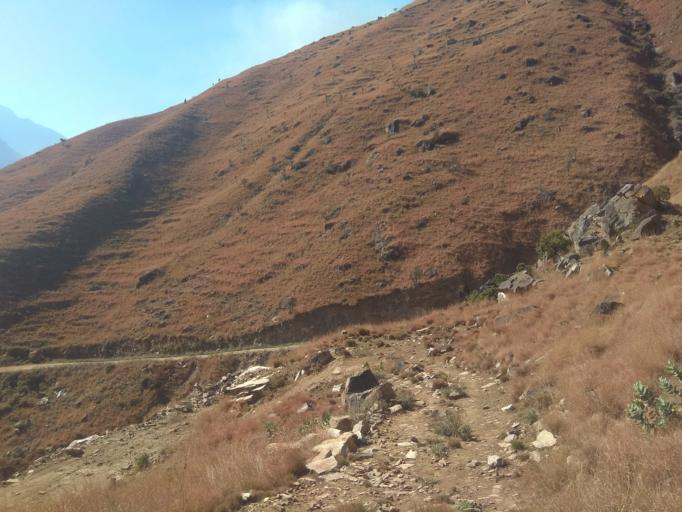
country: NP
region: Mid Western
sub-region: Karnali Zone
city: Jumla
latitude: 29.3065
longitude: 81.7450
